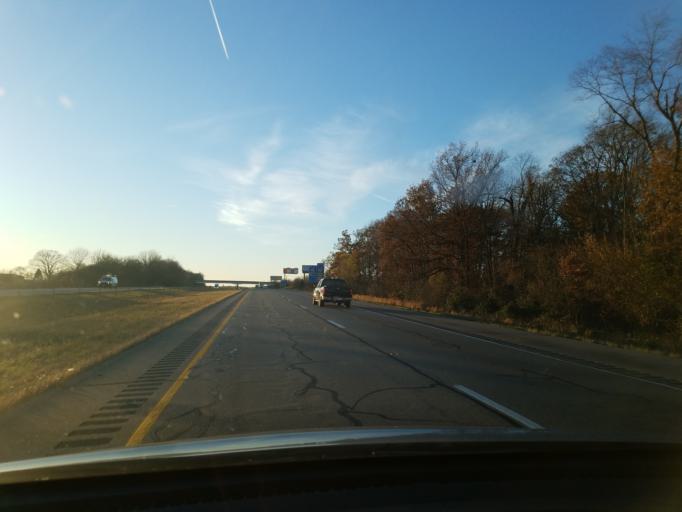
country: US
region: Indiana
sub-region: Gibson County
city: Haubstadt
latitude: 38.1665
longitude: -87.5258
